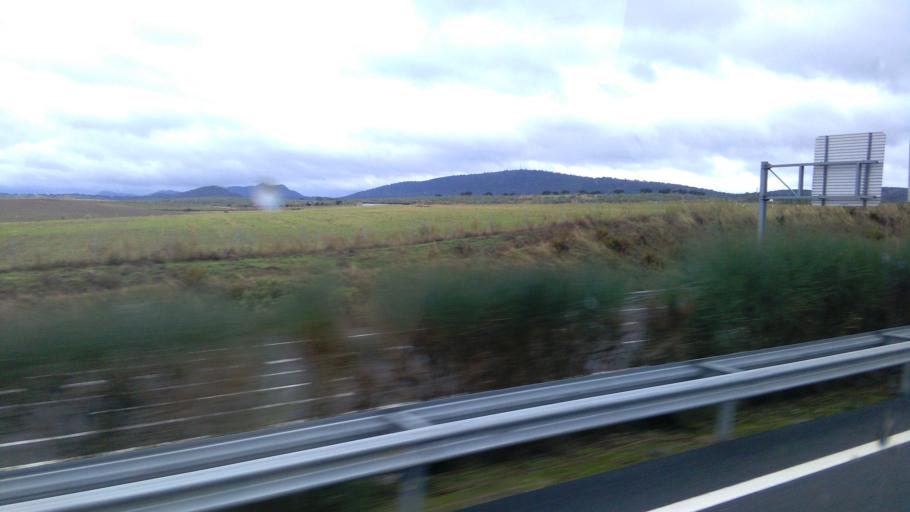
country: ES
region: Extremadura
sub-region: Provincia de Caceres
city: Saucedilla
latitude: 39.8355
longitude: -5.6509
